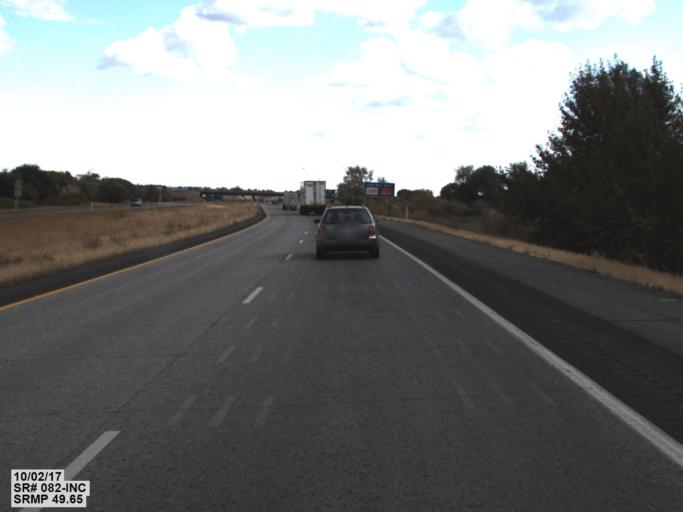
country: US
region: Washington
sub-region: Yakima County
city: Toppenish
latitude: 46.4174
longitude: -120.3233
